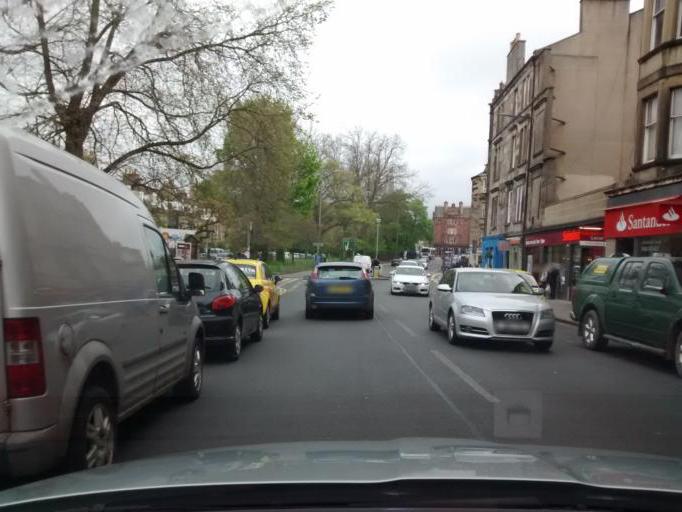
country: GB
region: Scotland
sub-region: Edinburgh
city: Edinburgh
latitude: 55.9270
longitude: -3.2092
